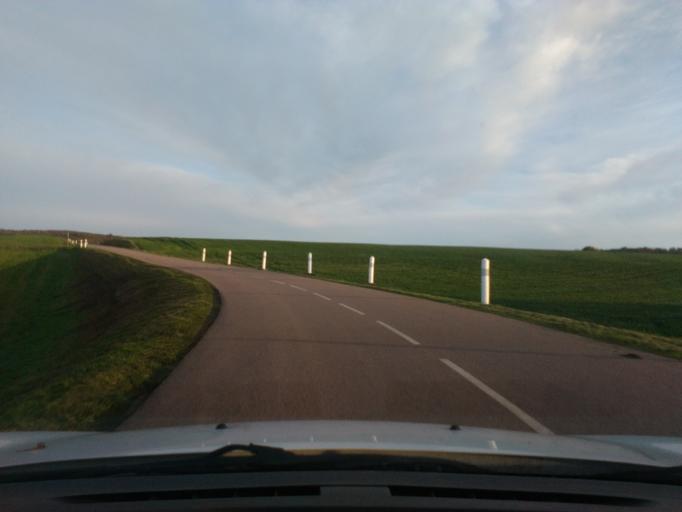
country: FR
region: Lorraine
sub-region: Departement des Vosges
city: Mirecourt
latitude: 48.2235
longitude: 6.1513
